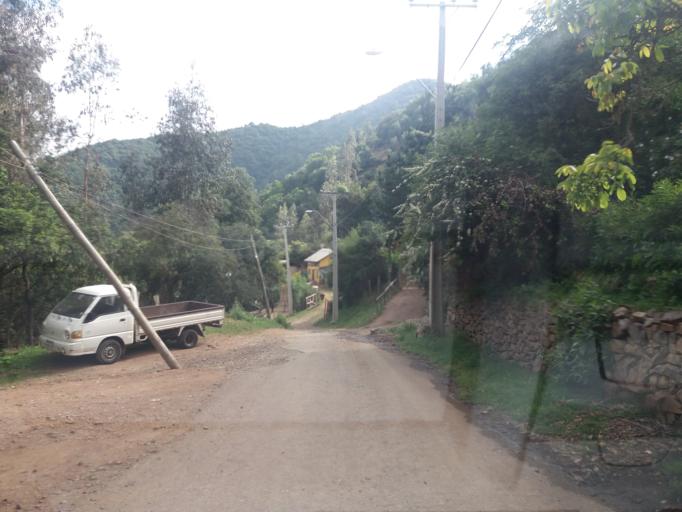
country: CL
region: Valparaiso
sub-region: Provincia de Marga Marga
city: Limache
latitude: -33.0736
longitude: -71.0613
